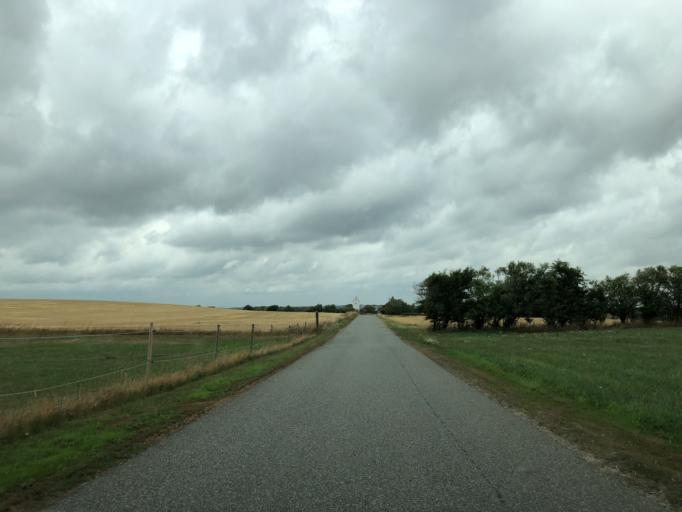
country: DK
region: Central Jutland
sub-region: Ringkobing-Skjern Kommune
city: Videbaek
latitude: 56.1075
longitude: 8.4988
